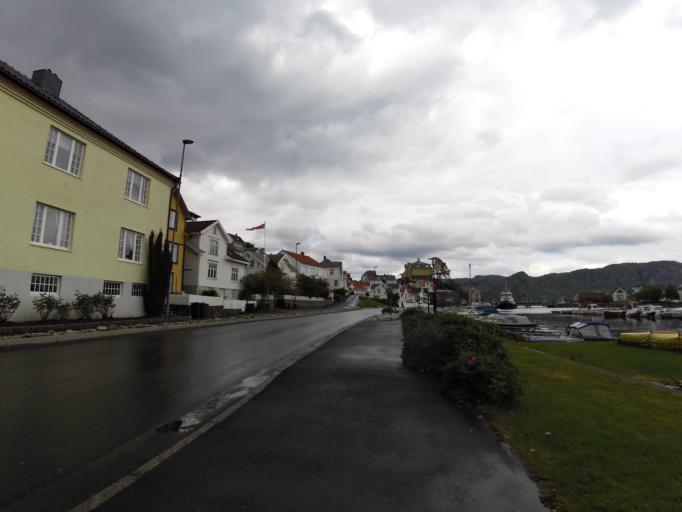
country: NO
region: Vest-Agder
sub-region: Farsund
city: Farsund
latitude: 58.0909
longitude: 6.8054
